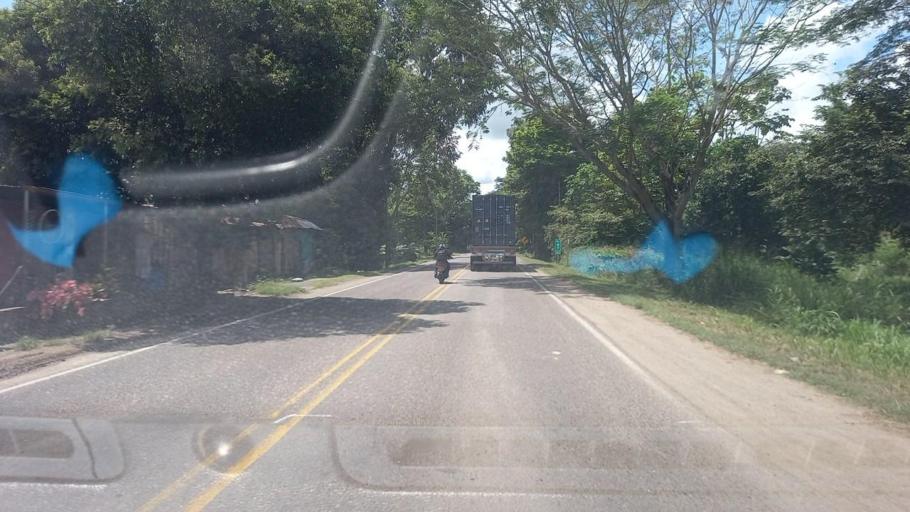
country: CO
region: Santander
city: Puerto Parra
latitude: 6.7279
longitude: -73.8701
